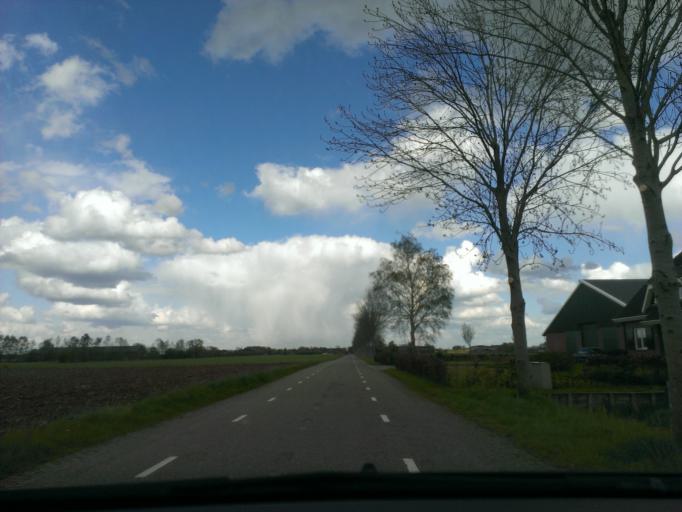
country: NL
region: Gelderland
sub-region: Gemeente Voorst
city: Twello
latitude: 52.2591
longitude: 6.0476
